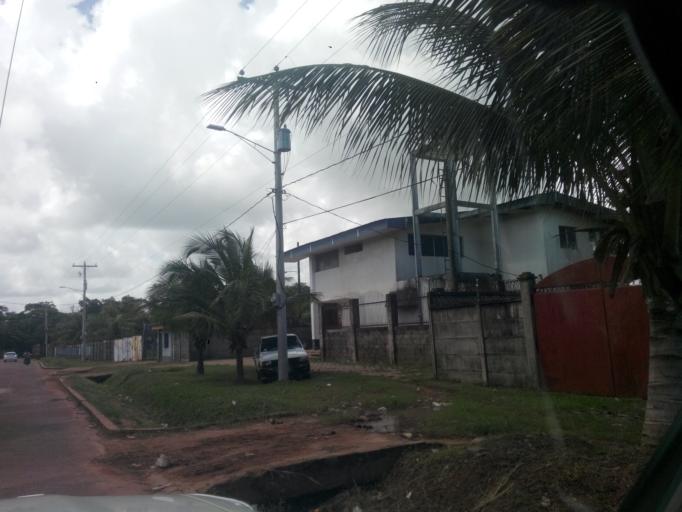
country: NI
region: Atlantico Norte (RAAN)
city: Puerto Cabezas
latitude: 14.0383
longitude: -83.3876
